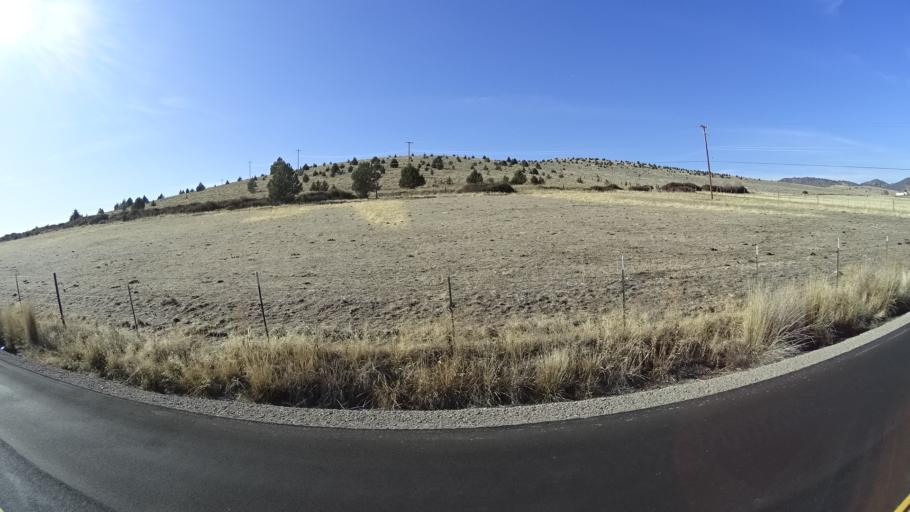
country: US
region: California
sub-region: Siskiyou County
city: Montague
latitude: 41.6030
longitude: -122.5306
